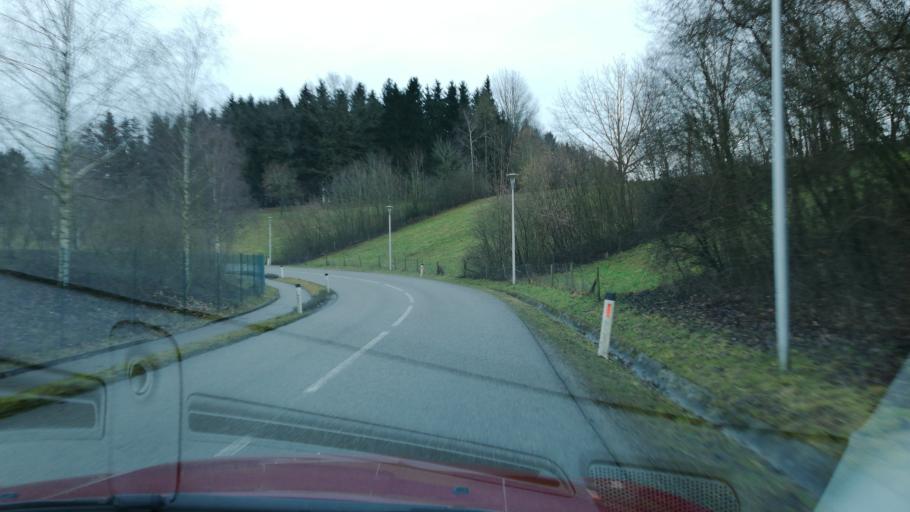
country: AT
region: Upper Austria
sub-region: Politischer Bezirk Braunau am Inn
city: Altheim
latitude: 48.2607
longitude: 13.2957
